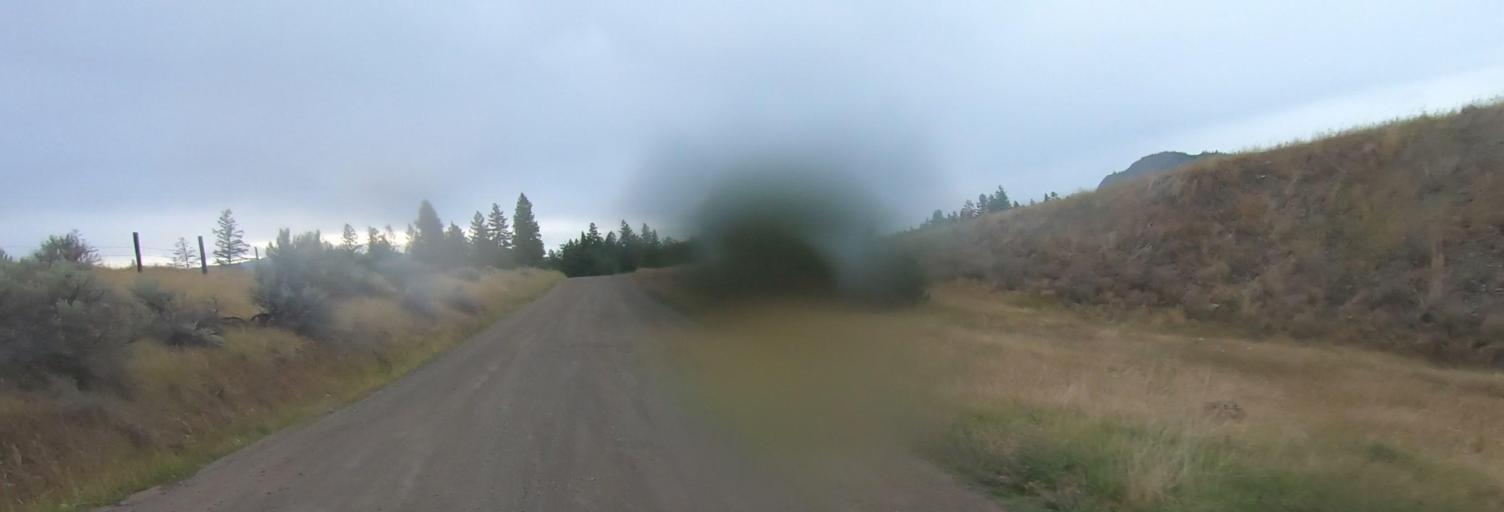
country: CA
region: British Columbia
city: Kamloops
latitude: 50.6169
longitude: -120.4445
